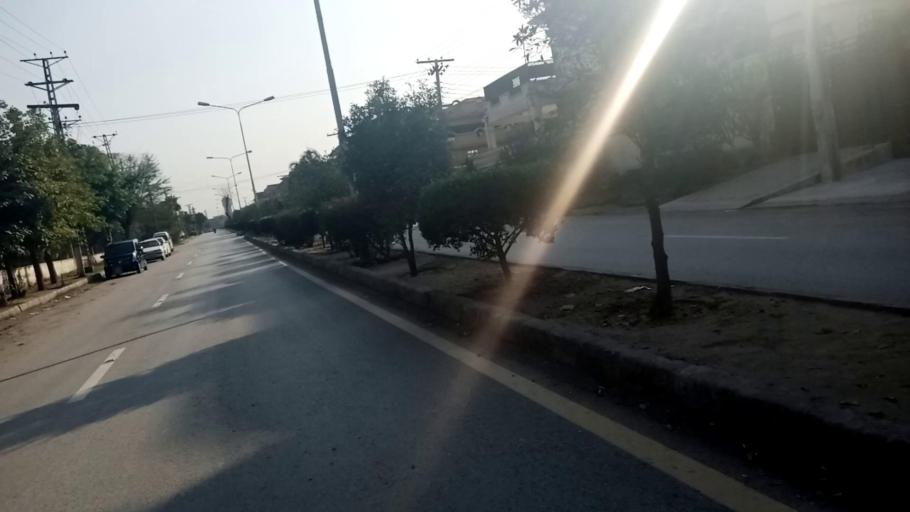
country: PK
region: Khyber Pakhtunkhwa
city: Peshawar
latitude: 33.9920
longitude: 71.4459
